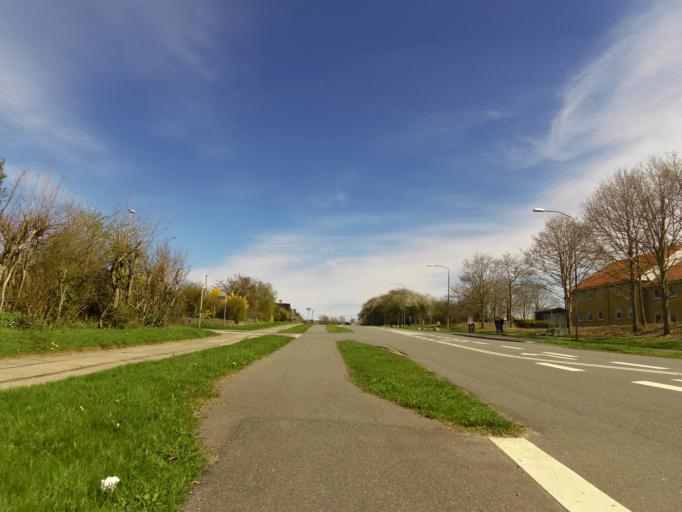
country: DK
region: Central Jutland
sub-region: Skive Kommune
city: Skive
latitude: 56.5856
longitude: 9.0295
